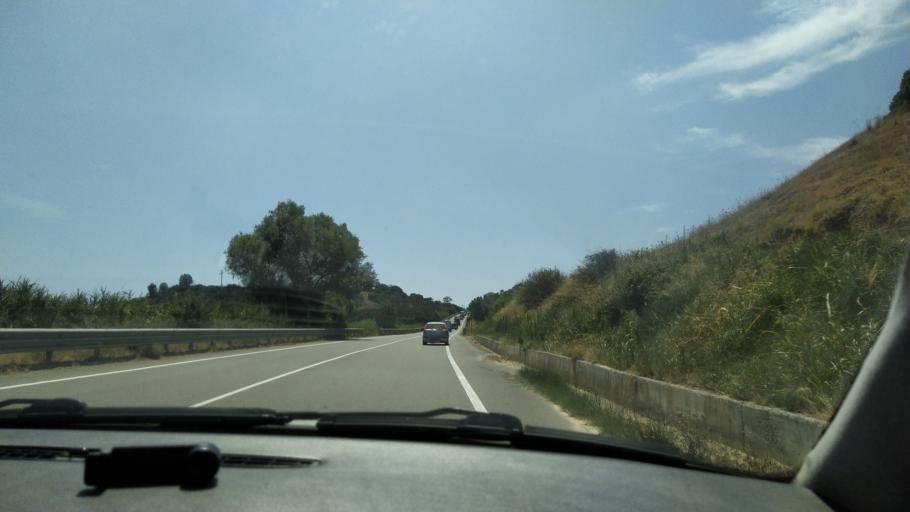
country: IT
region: Apulia
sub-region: Provincia di Taranto
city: Marina di Ginosa
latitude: 40.4309
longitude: 16.7933
